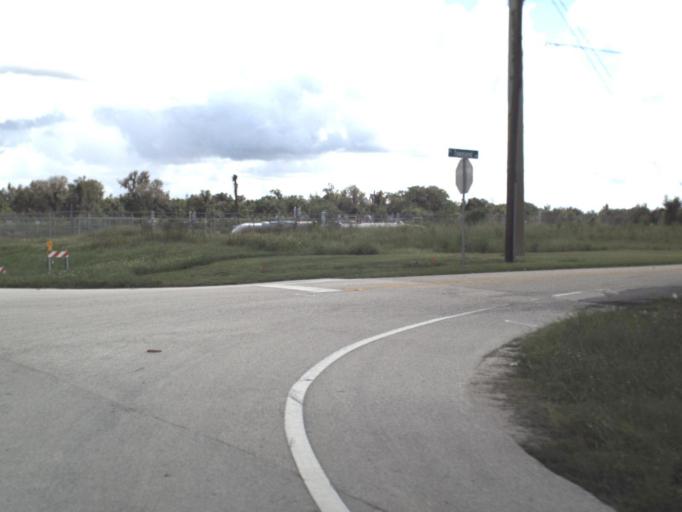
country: US
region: Florida
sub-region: DeSoto County
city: Southeast Arcadia
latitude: 27.2088
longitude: -81.8084
